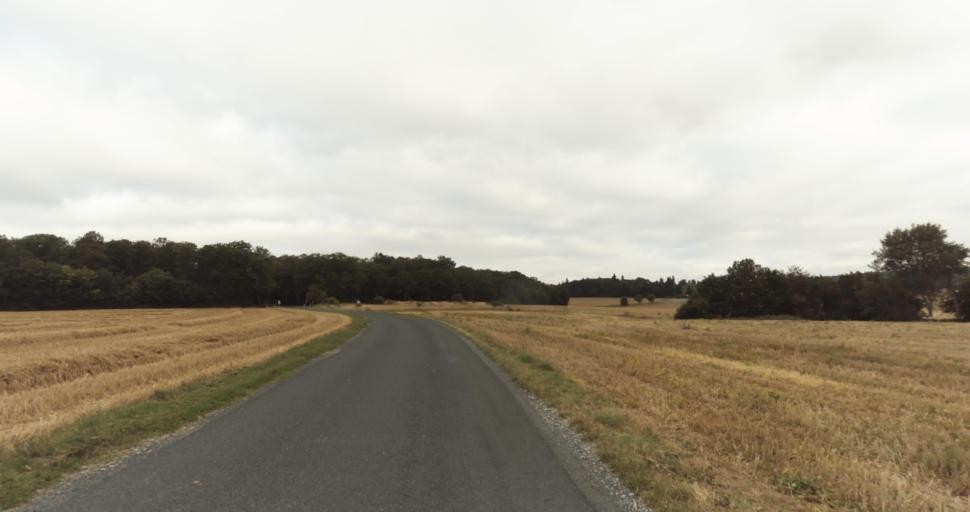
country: FR
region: Centre
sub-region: Departement d'Eure-et-Loir
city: Saint-Remy-sur-Avre
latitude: 48.7766
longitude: 1.2458
